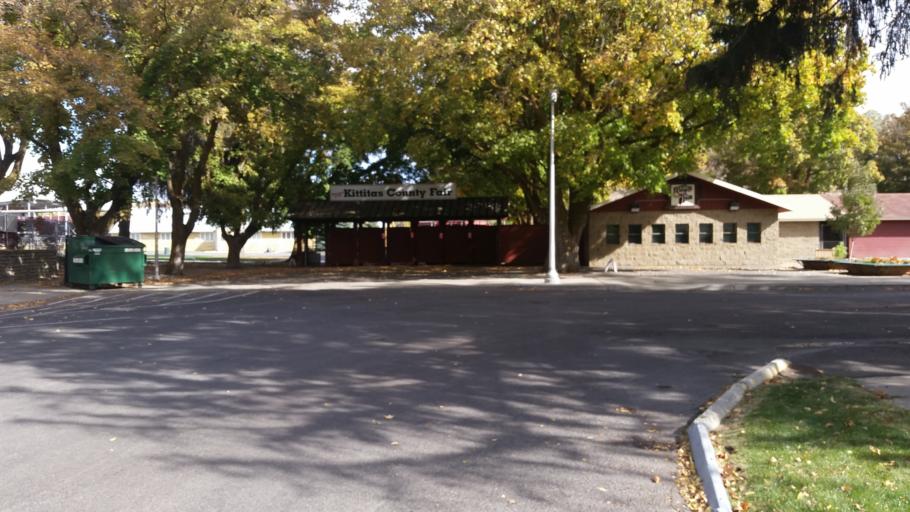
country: US
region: Washington
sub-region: Kittitas County
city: Ellensburg
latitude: 46.9978
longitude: -120.5356
